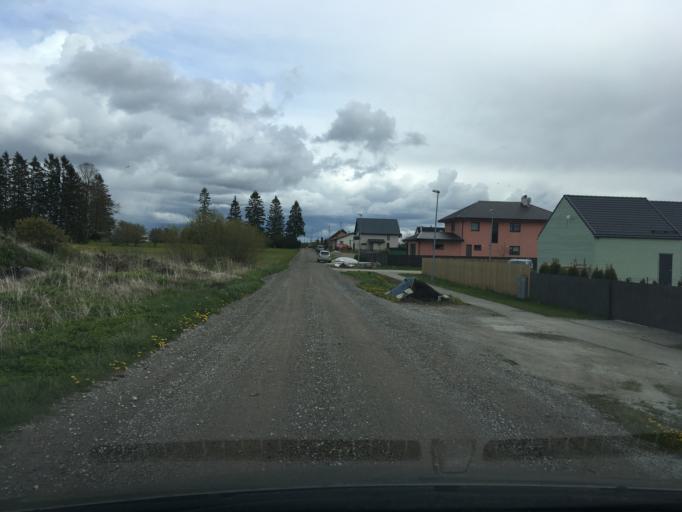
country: EE
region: Harju
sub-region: Joelaehtme vald
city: Loo
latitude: 59.4055
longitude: 24.9467
